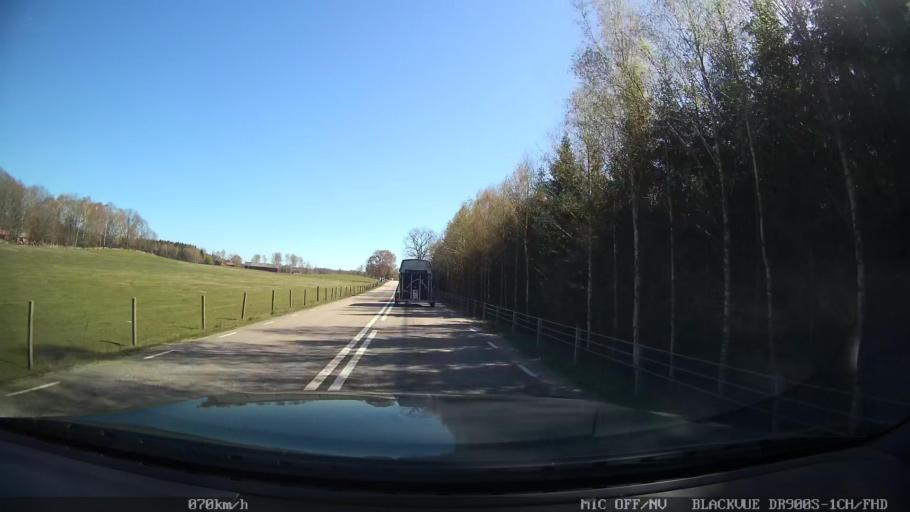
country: SE
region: Skane
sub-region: Klippans Kommun
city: Ljungbyhed
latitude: 56.0988
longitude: 13.1812
